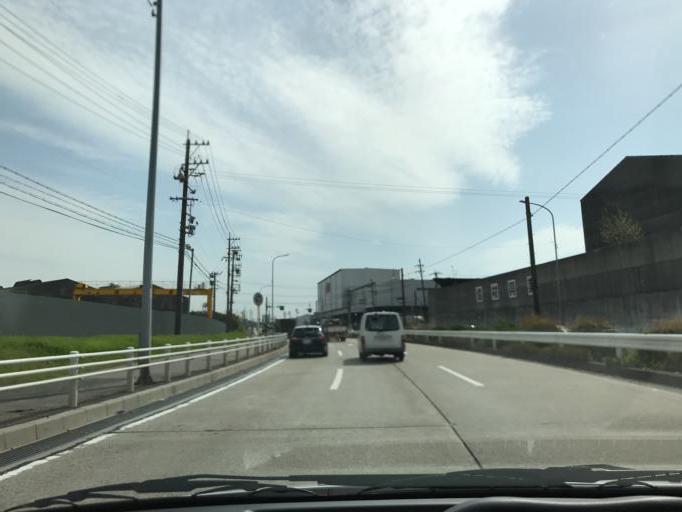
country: JP
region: Aichi
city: Obu
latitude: 35.0616
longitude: 136.9057
